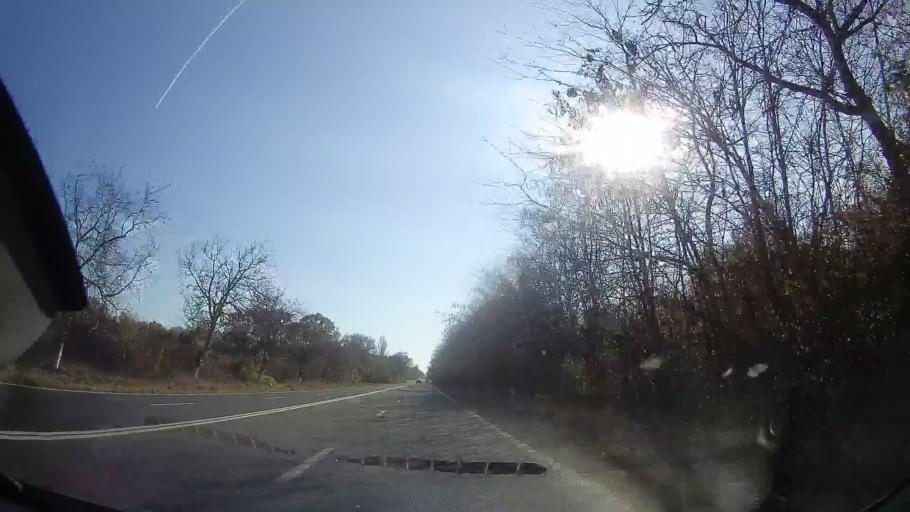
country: RO
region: Constanta
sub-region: Comuna Douazeci si Trei August
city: Dulcesti
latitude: 43.8787
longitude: 28.5736
